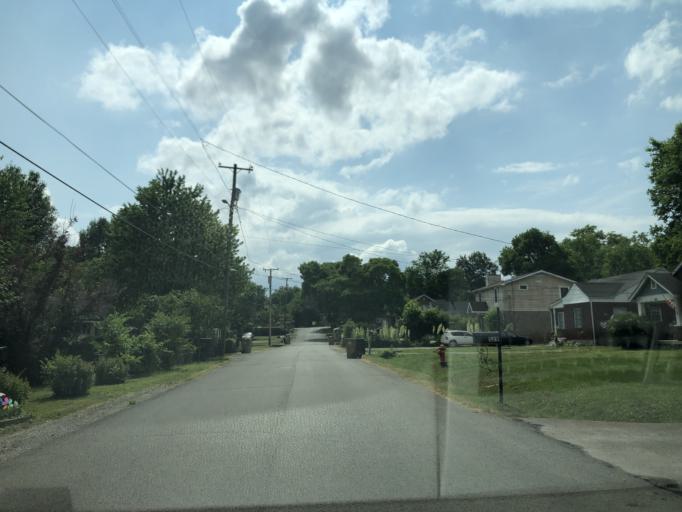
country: US
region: Tennessee
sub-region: Davidson County
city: Goodlettsville
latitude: 36.2614
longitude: -86.7014
